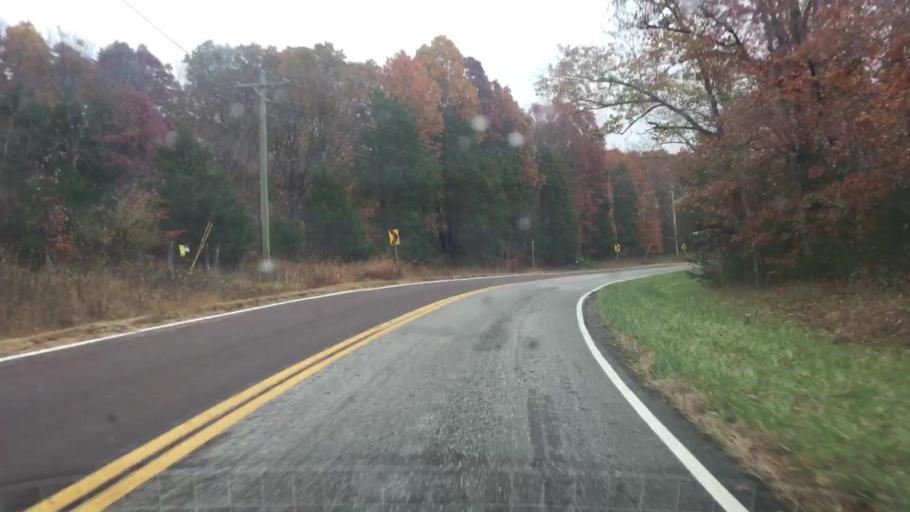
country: US
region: Missouri
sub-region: Callaway County
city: Fulton
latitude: 38.7824
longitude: -91.8274
